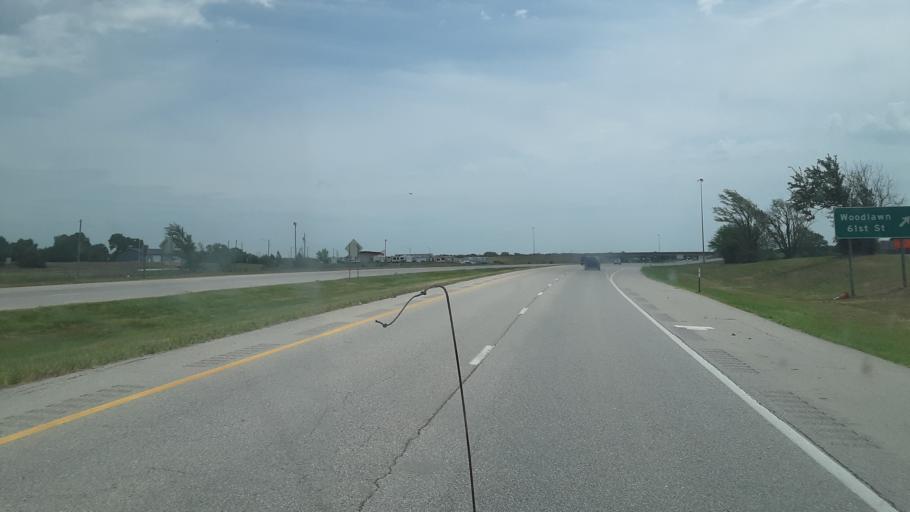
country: US
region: Kansas
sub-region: Sedgwick County
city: Kechi
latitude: 37.7956
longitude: -97.2692
